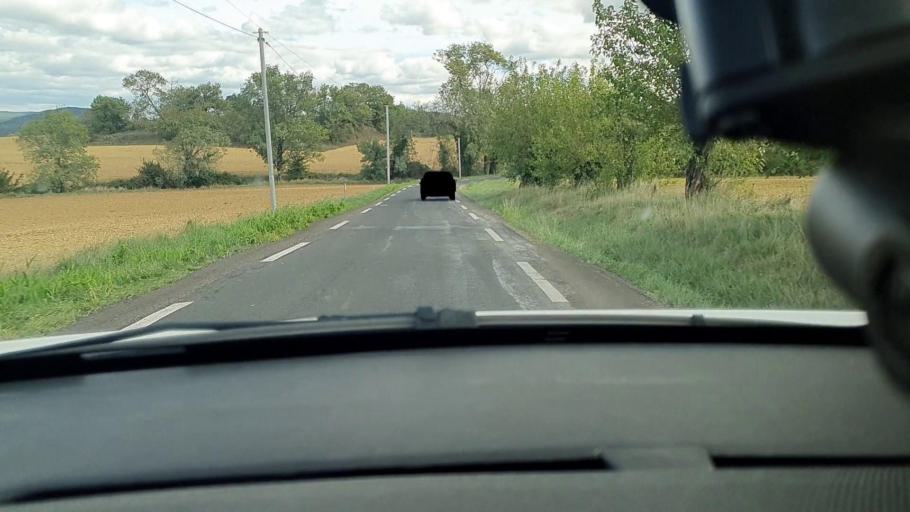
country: FR
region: Languedoc-Roussillon
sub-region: Departement du Gard
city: Les Mages
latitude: 44.1969
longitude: 4.2112
